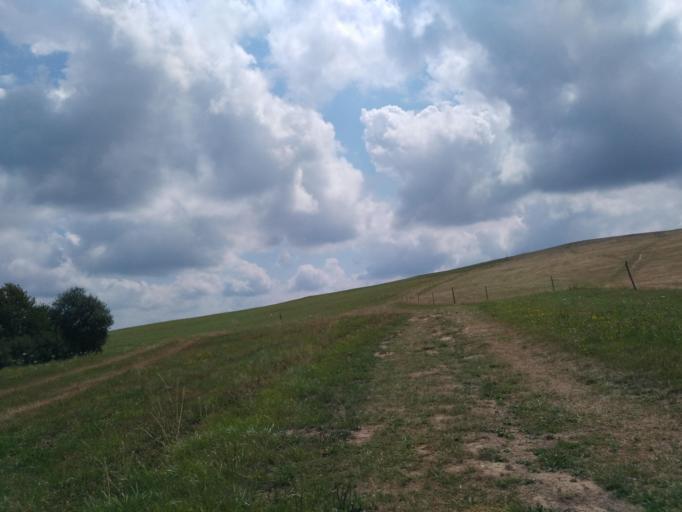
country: PL
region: Subcarpathian Voivodeship
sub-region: Powiat krosnienski
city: Iwonicz-Zdroj
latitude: 49.5811
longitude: 21.7775
